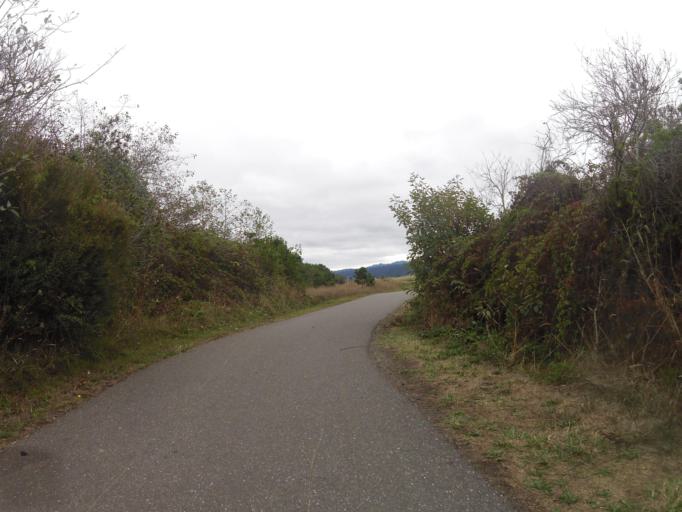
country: US
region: California
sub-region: Humboldt County
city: Bayview
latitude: 40.7622
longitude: -124.1960
